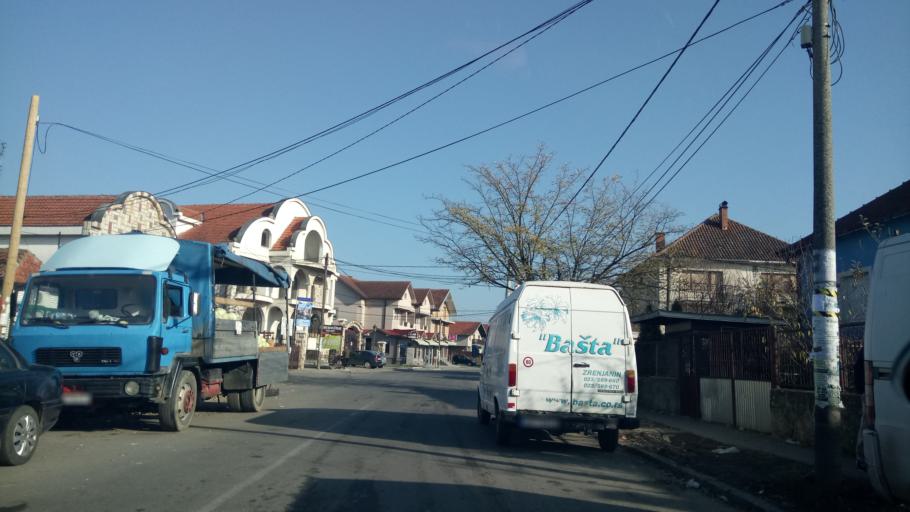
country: RS
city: Novi Banovci
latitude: 44.9053
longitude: 20.2852
